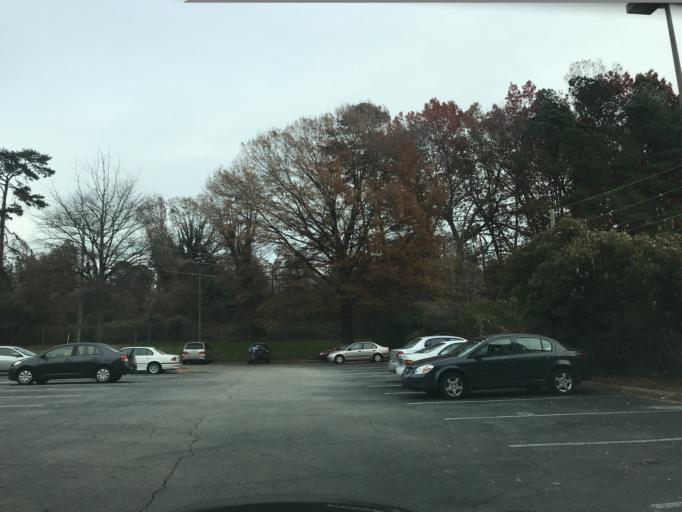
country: US
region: North Carolina
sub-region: Wake County
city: West Raleigh
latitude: 35.7869
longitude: -78.7003
